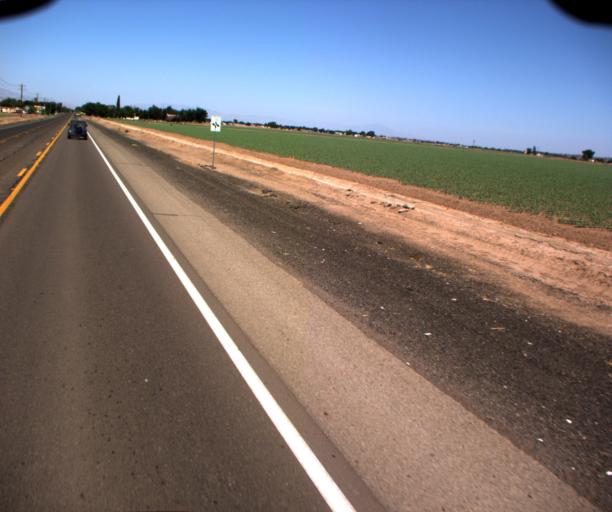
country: US
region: Arizona
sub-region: Graham County
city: Safford
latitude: 32.8167
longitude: -109.6653
